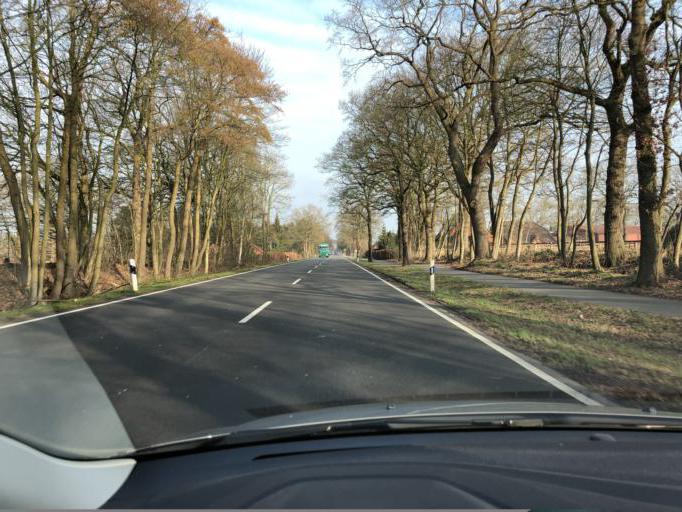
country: DE
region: Lower Saxony
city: Hesel
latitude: 53.3142
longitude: 7.5968
